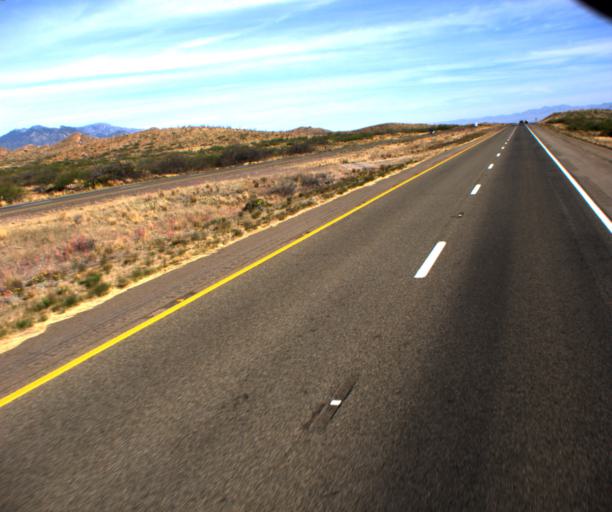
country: US
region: Arizona
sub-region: Graham County
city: Swift Trail Junction
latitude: 32.5010
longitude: -109.6737
